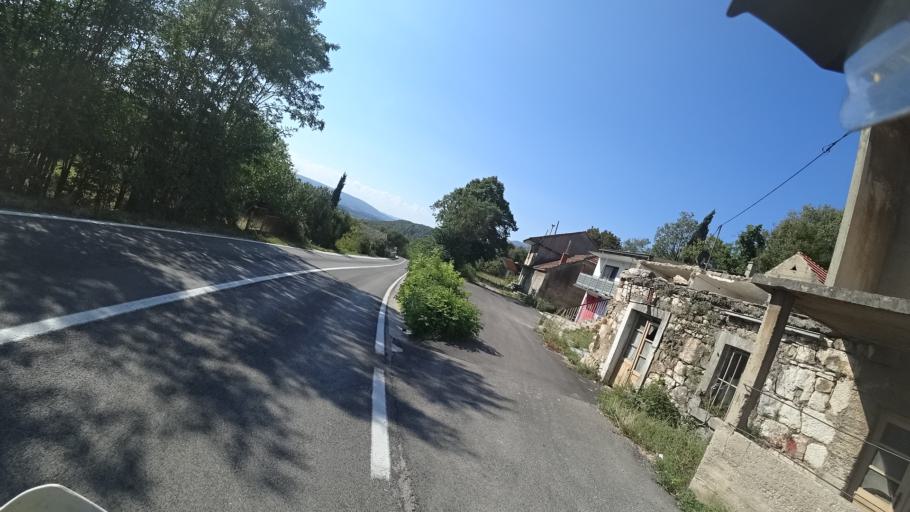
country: HR
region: Sibensko-Kniniska
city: Knin
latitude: 44.0144
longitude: 16.1972
